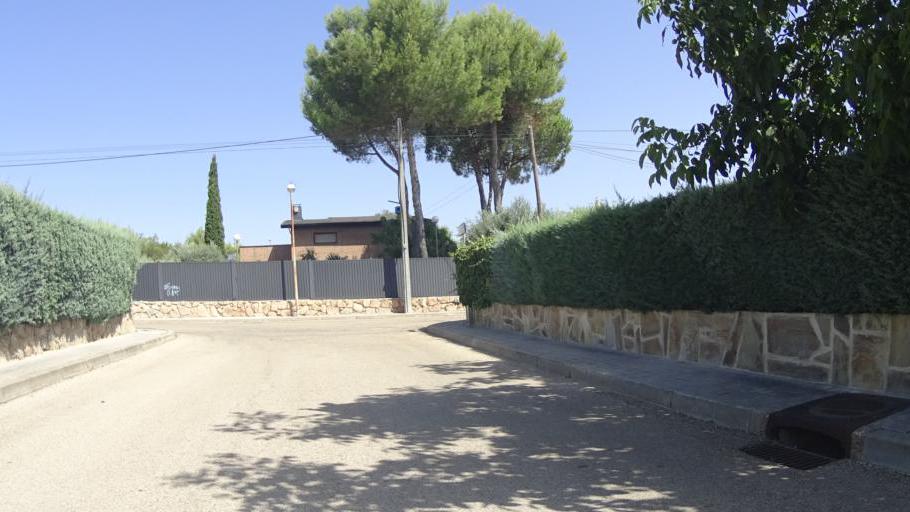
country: ES
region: Madrid
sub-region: Provincia de Madrid
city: Colmenarejo
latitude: 40.5598
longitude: -4.0068
